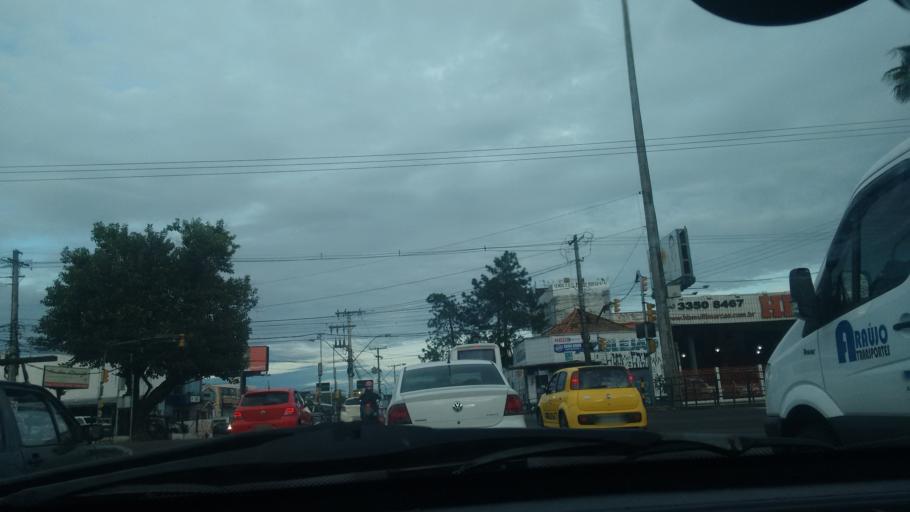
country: BR
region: Rio Grande do Sul
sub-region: Cachoeirinha
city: Cachoeirinha
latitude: -29.9998
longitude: -51.1326
